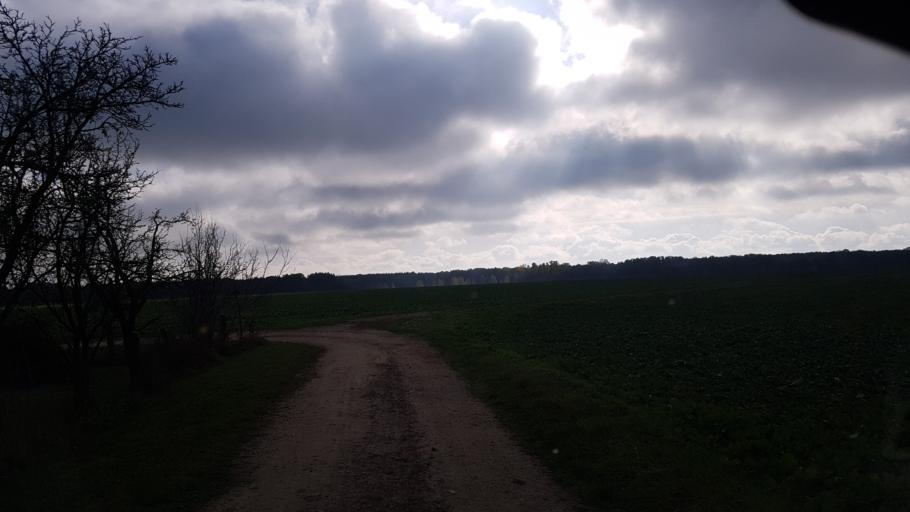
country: DE
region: Brandenburg
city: Doberlug-Kirchhain
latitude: 51.6530
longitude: 13.5259
